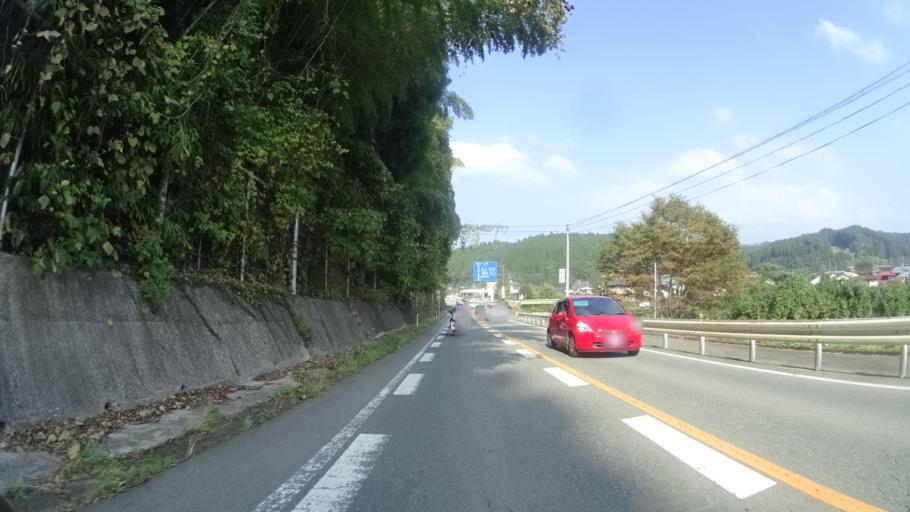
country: JP
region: Kumamoto
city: Aso
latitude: 33.0959
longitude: 131.0668
